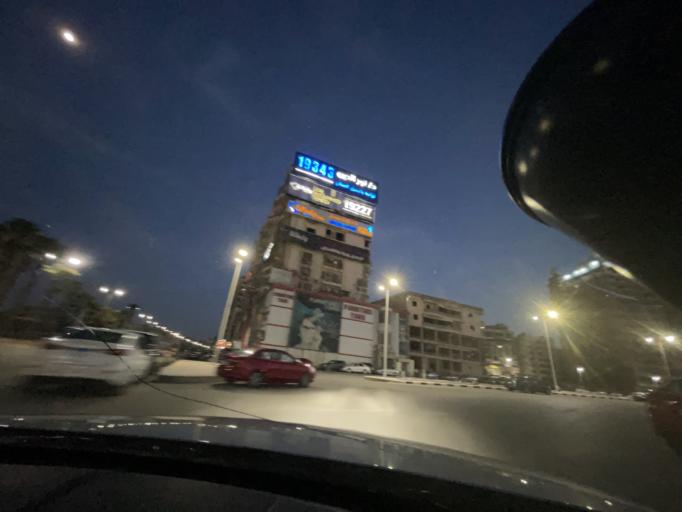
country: EG
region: Muhafazat al Qahirah
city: Cairo
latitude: 30.0701
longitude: 31.3551
